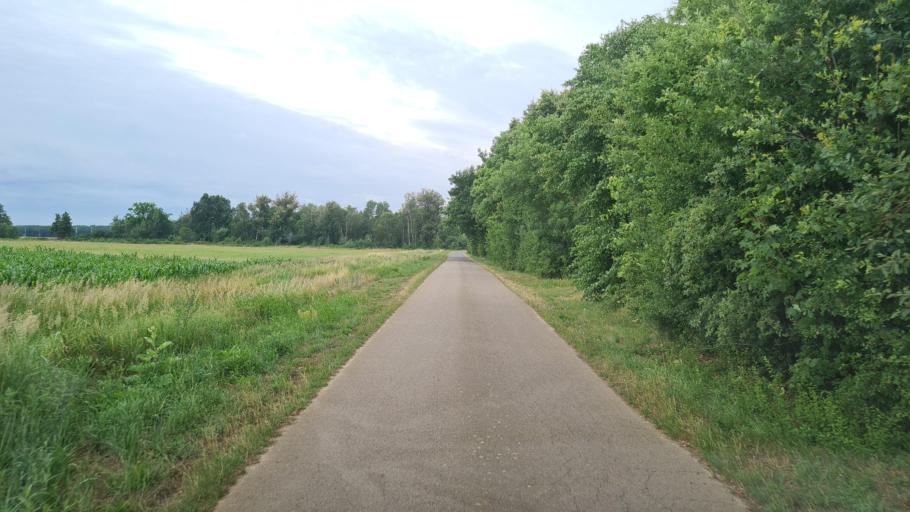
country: DE
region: Saxony-Anhalt
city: Annaburg
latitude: 51.7508
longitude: 13.0123
